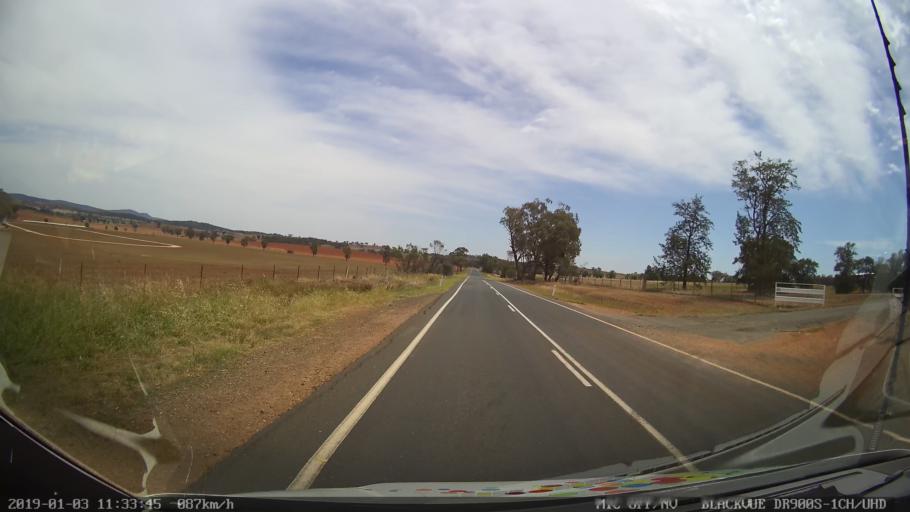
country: AU
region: New South Wales
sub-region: Weddin
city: Grenfell
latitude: -33.9432
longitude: 148.1687
